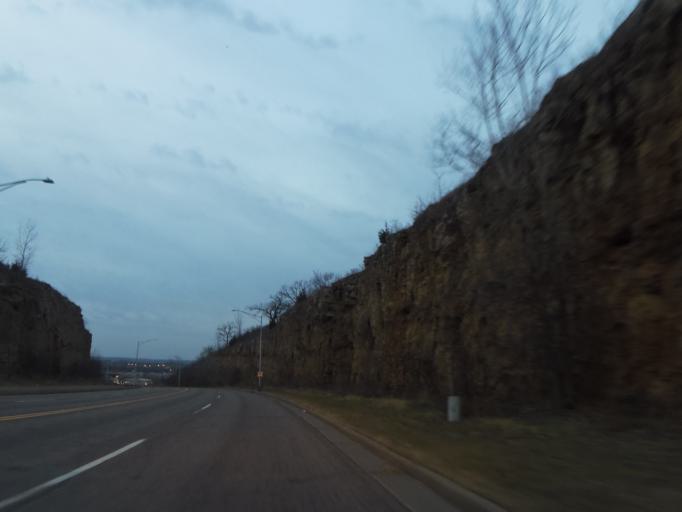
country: US
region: Wisconsin
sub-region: Saint Croix County
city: Hudson
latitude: 44.9542
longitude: -92.7153
